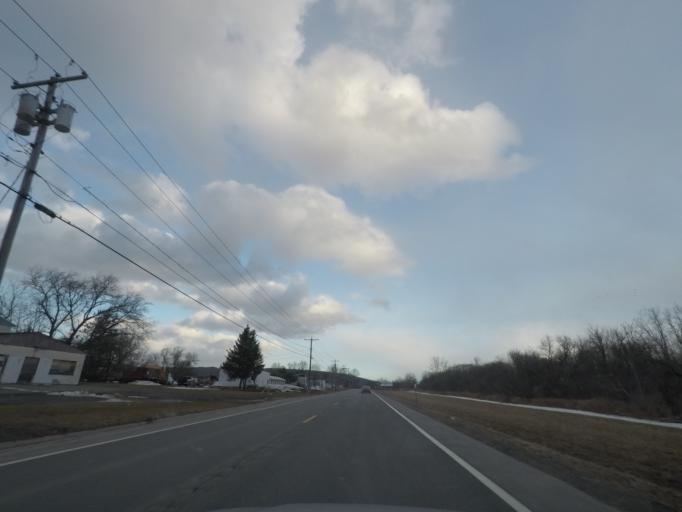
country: US
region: New York
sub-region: Herkimer County
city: Frankfort
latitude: 43.0606
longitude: -75.0857
